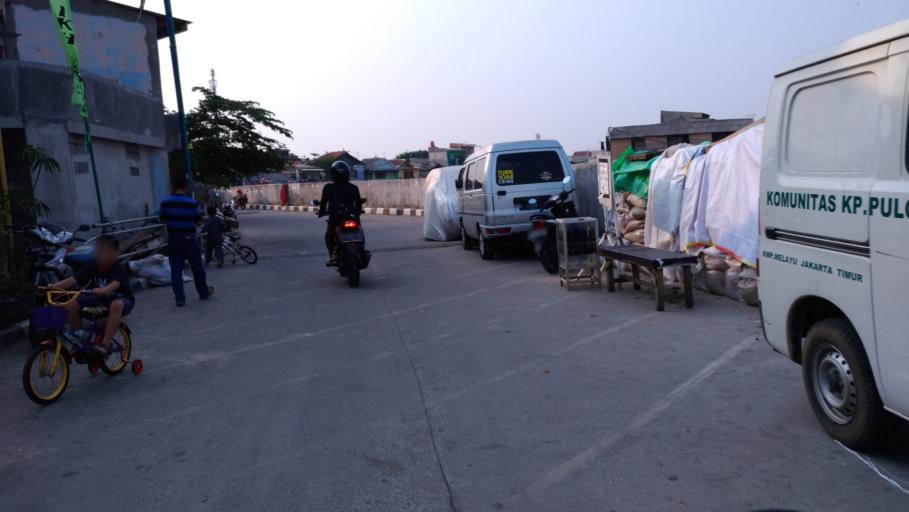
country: ID
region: Jakarta Raya
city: Jakarta
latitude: -6.2211
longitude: 106.8616
